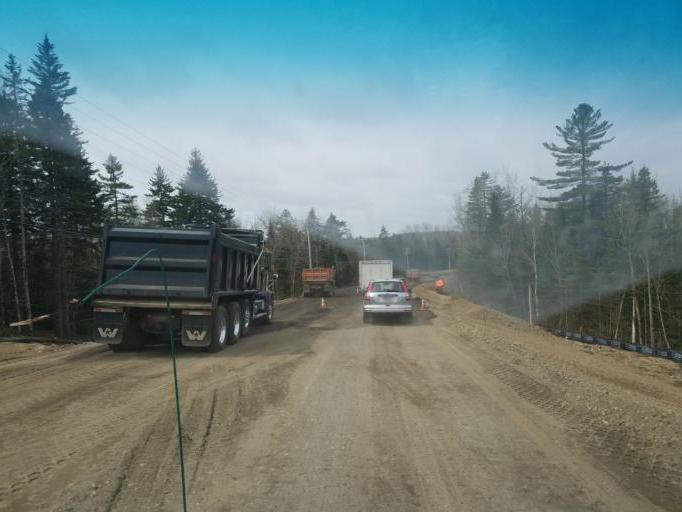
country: US
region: Maine
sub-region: Washington County
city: East Machias
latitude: 44.7671
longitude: -67.1994
